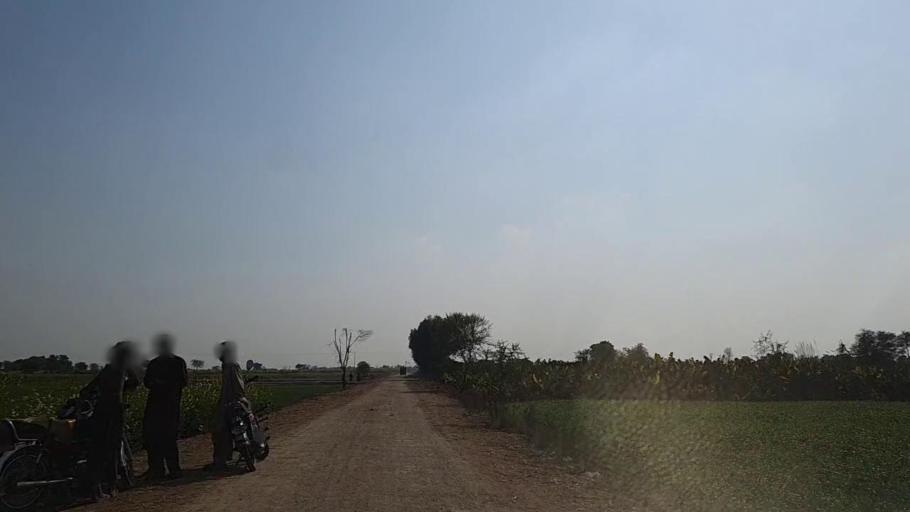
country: PK
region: Sindh
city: Daur
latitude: 26.4231
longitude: 68.2368
